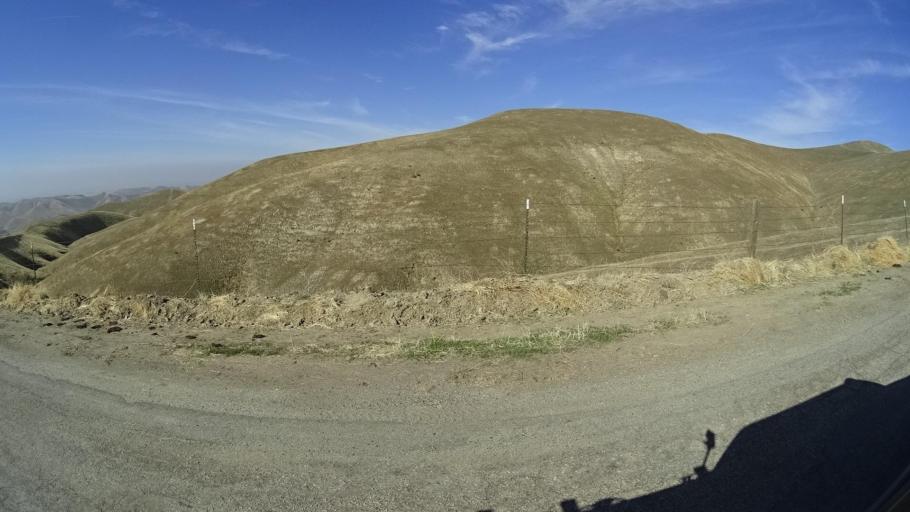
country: US
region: California
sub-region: Kern County
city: Lamont
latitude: 35.4012
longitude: -118.7737
